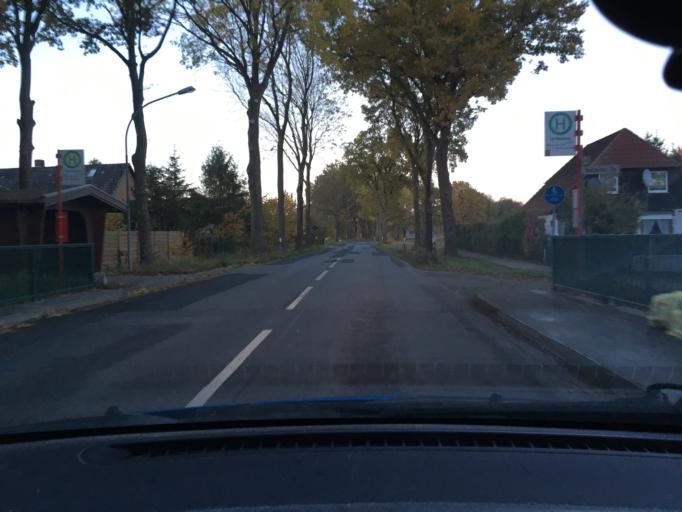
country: DE
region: Lower Saxony
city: Radbruch
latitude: 53.3274
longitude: 10.2977
